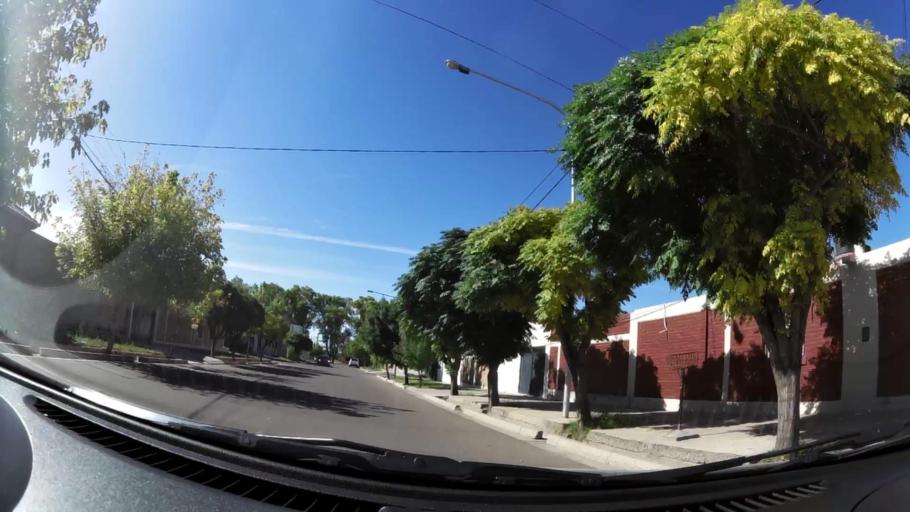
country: AR
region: Mendoza
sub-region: Departamento de Godoy Cruz
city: Godoy Cruz
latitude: -32.9456
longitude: -68.8141
